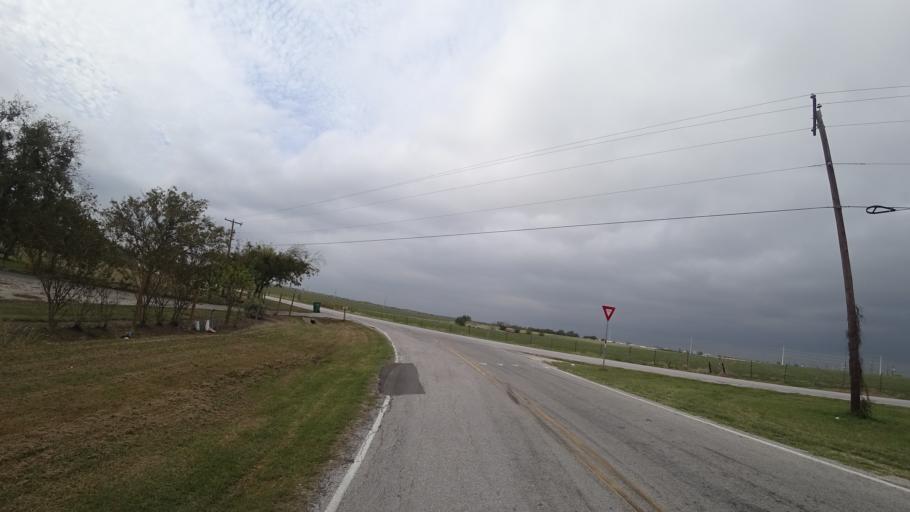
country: US
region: Texas
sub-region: Travis County
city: Pflugerville
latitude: 30.4168
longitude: -97.5760
